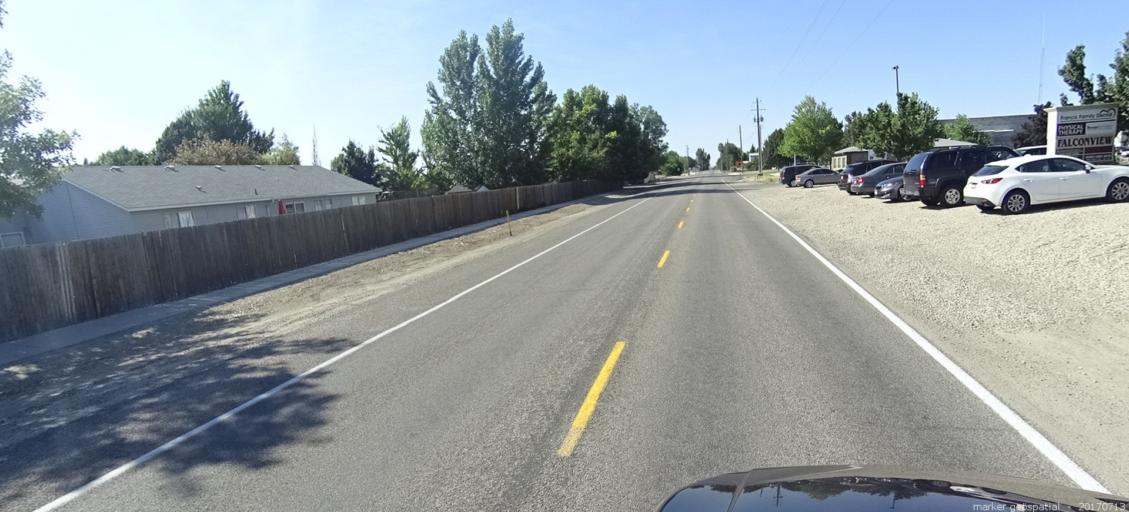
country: US
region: Idaho
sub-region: Ada County
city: Kuna
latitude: 43.4977
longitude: -116.4137
